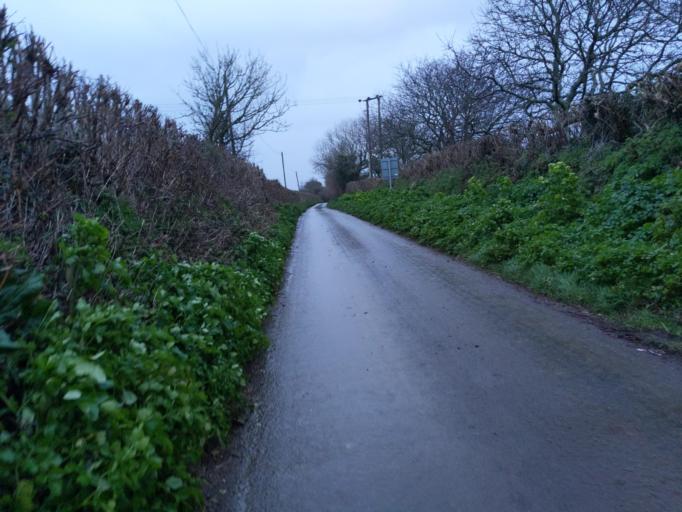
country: GB
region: England
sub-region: Devon
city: Yealmpton
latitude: 50.3240
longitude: -4.0304
